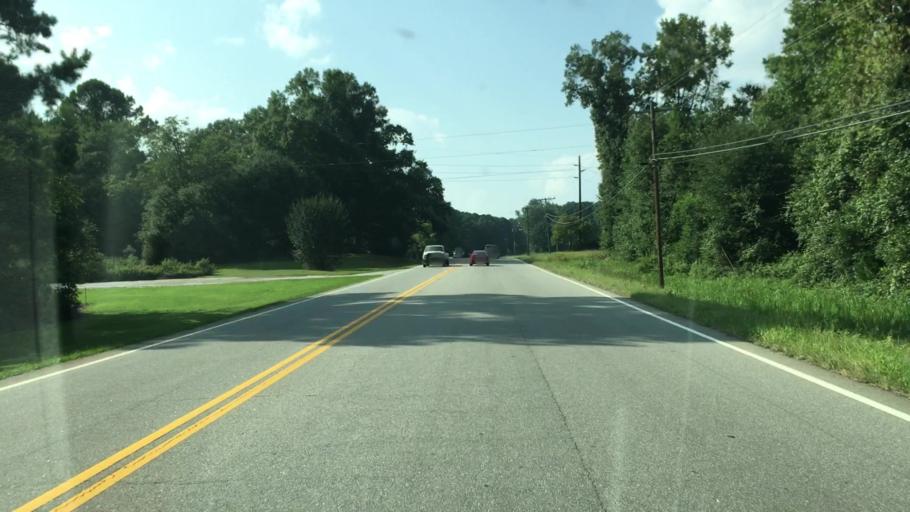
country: US
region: Georgia
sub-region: Walton County
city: Monroe
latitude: 33.7313
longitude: -83.6982
